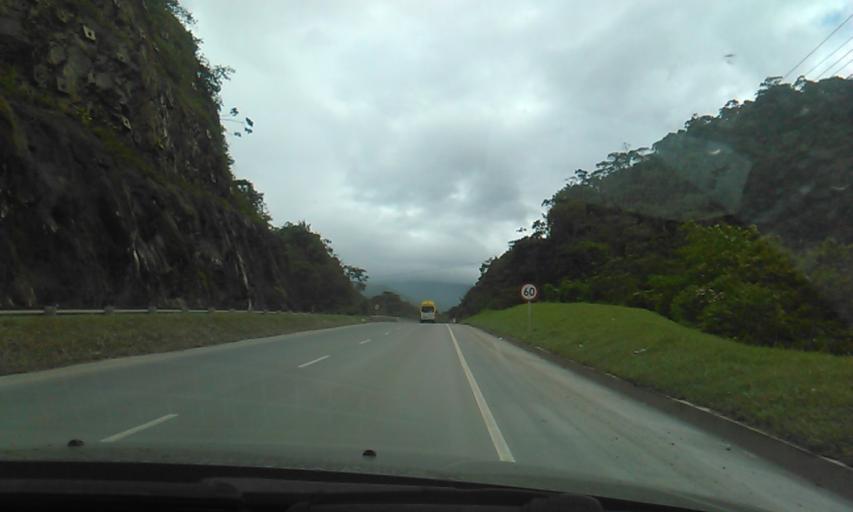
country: CO
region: Valle del Cauca
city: Dagua
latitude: 3.8305
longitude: -76.7883
